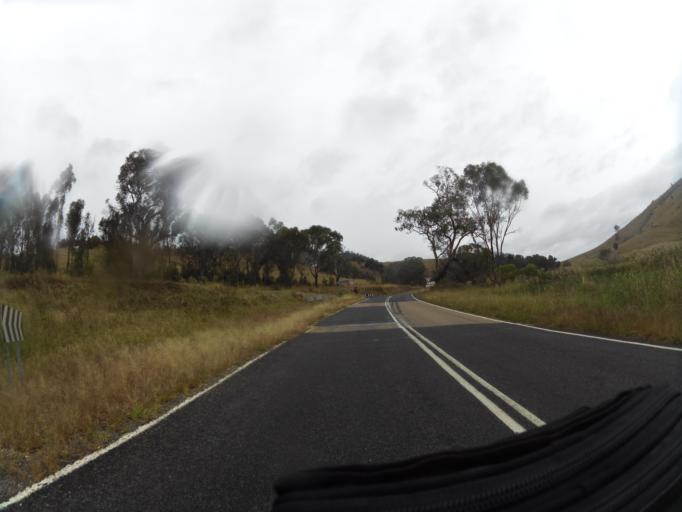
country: AU
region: New South Wales
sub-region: Greater Hume Shire
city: Holbrook
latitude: -36.2209
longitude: 147.7296
